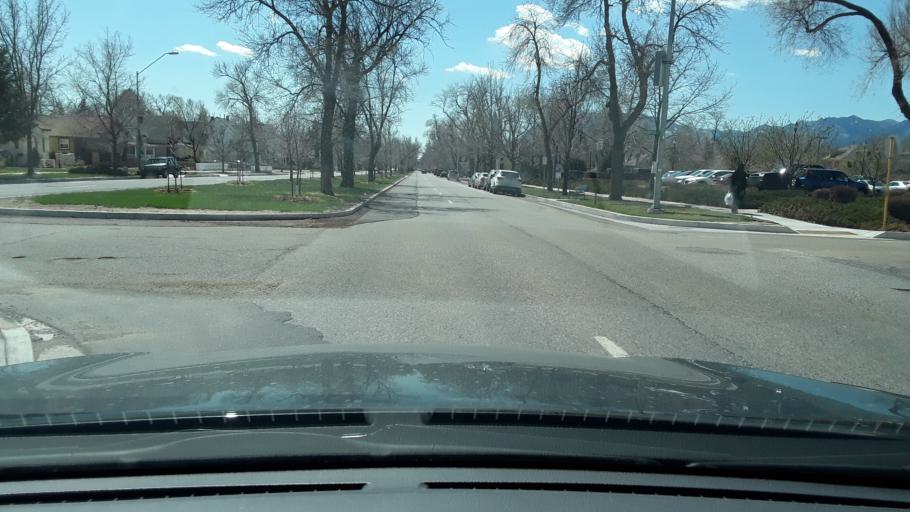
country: US
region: Colorado
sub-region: El Paso County
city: Colorado Springs
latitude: 38.8657
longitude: -104.8201
